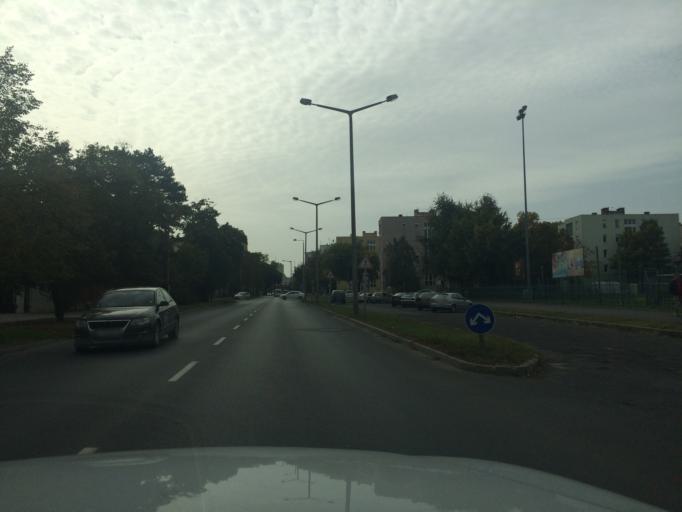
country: HU
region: Szabolcs-Szatmar-Bereg
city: Nyiregyhaza
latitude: 47.9692
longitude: 21.7152
